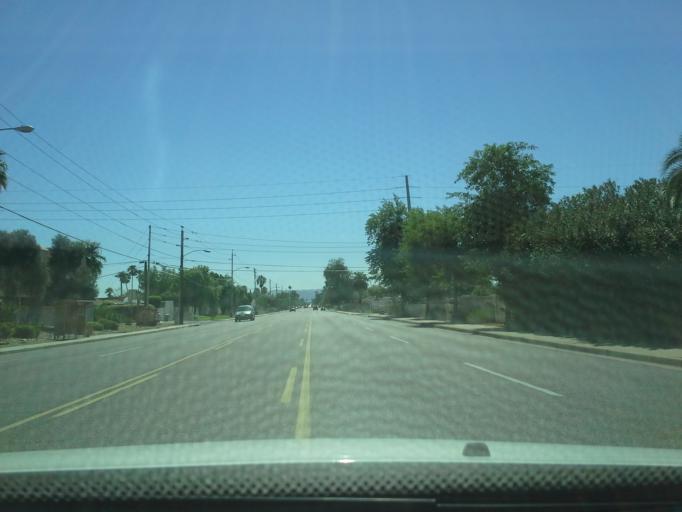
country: US
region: Arizona
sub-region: Maricopa County
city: Phoenix
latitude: 33.5354
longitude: -112.0475
